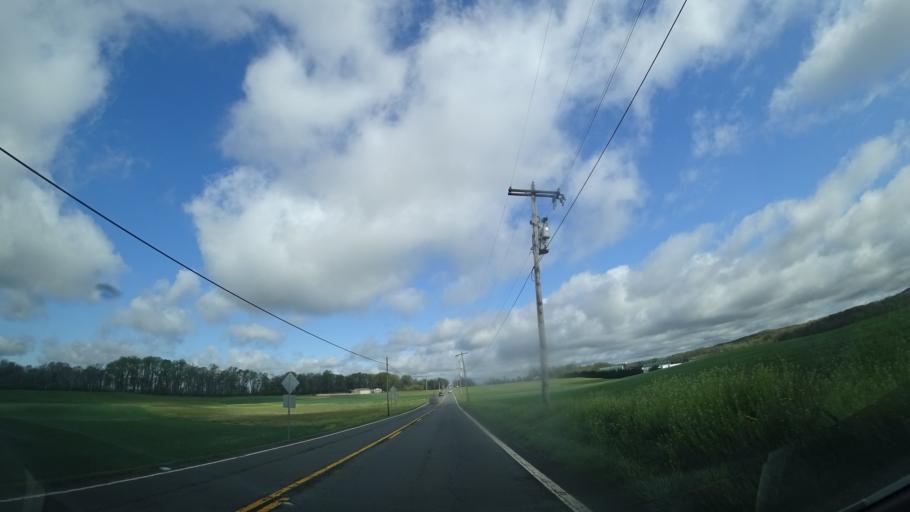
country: US
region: Maryland
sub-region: Montgomery County
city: Poolesville
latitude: 39.2260
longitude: -77.4272
